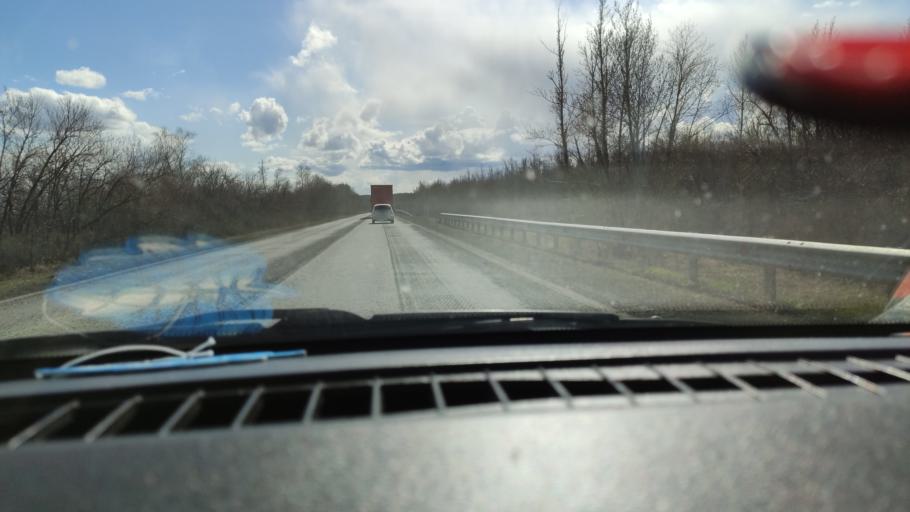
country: RU
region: Saratov
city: Dukhovnitskoye
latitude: 52.6702
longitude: 48.2211
